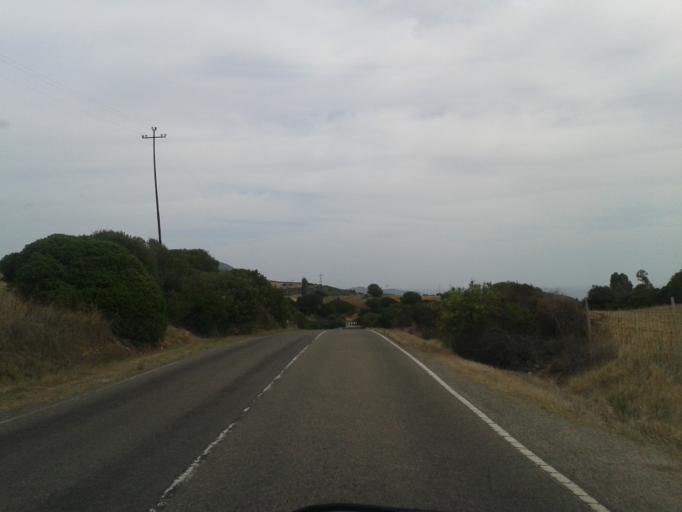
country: IT
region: Sardinia
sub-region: Provincia di Cagliari
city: Olia Speciosa
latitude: 39.2839
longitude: 9.5623
